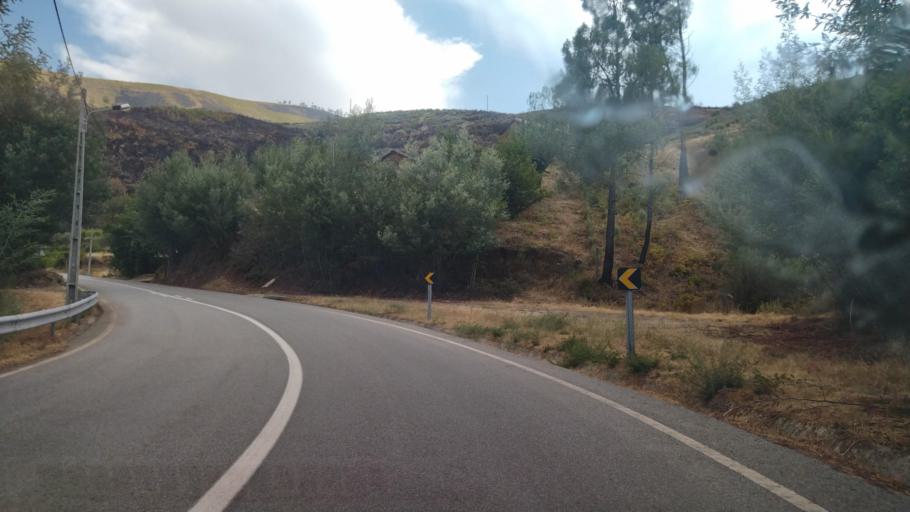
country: PT
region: Castelo Branco
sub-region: Covilha
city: Teixoso
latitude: 40.3722
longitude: -7.4568
